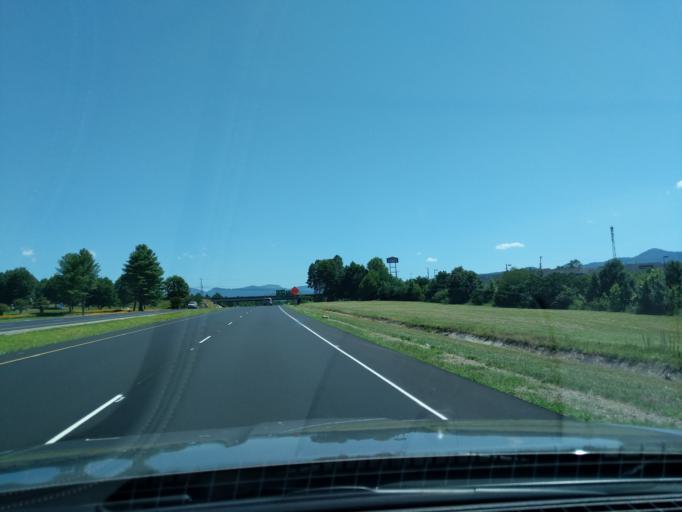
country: US
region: North Carolina
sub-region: Macon County
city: Franklin
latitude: 35.1667
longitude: -83.3950
